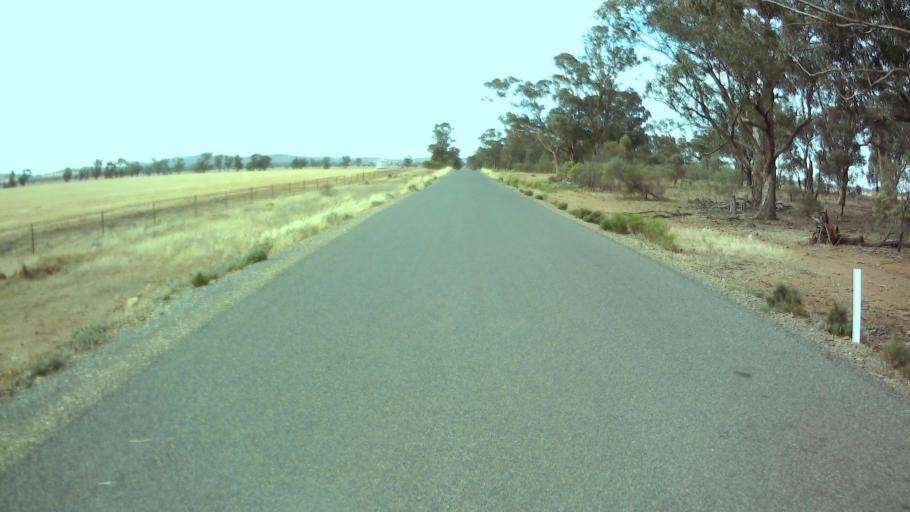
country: AU
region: New South Wales
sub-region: Weddin
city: Grenfell
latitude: -33.8870
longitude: 147.8549
